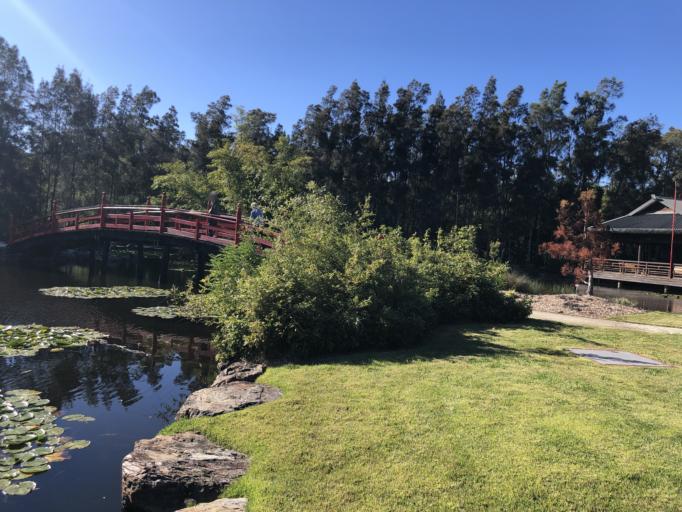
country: AU
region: New South Wales
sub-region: Coffs Harbour
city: Coffs Harbour
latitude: -30.2922
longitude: 153.1252
